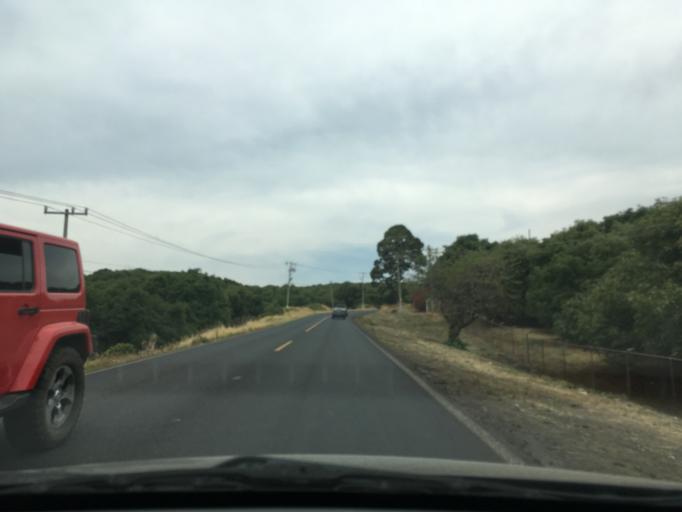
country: MX
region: Michoacan
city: Nuevo San Juan Parangaricutiro
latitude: 19.3994
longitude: -102.1078
